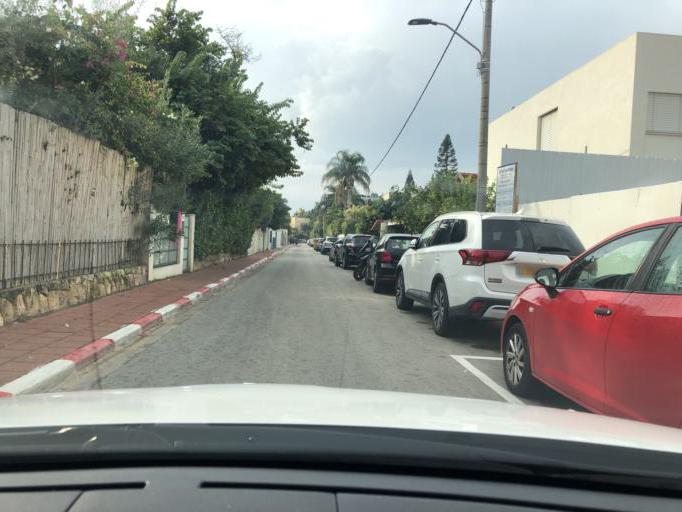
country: IL
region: Tel Aviv
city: Giv`atayim
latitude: 32.0556
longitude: 34.8192
